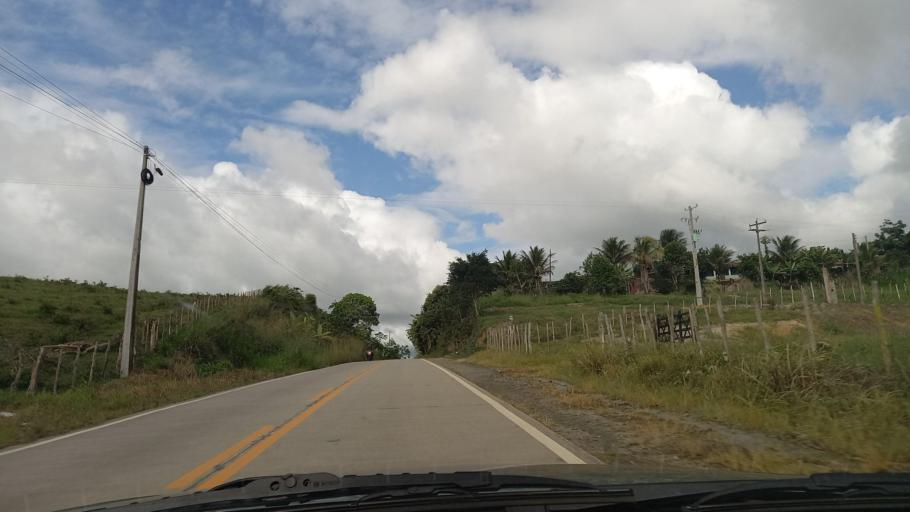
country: BR
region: Pernambuco
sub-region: Maraial
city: Maraial
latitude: -8.7880
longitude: -35.8987
